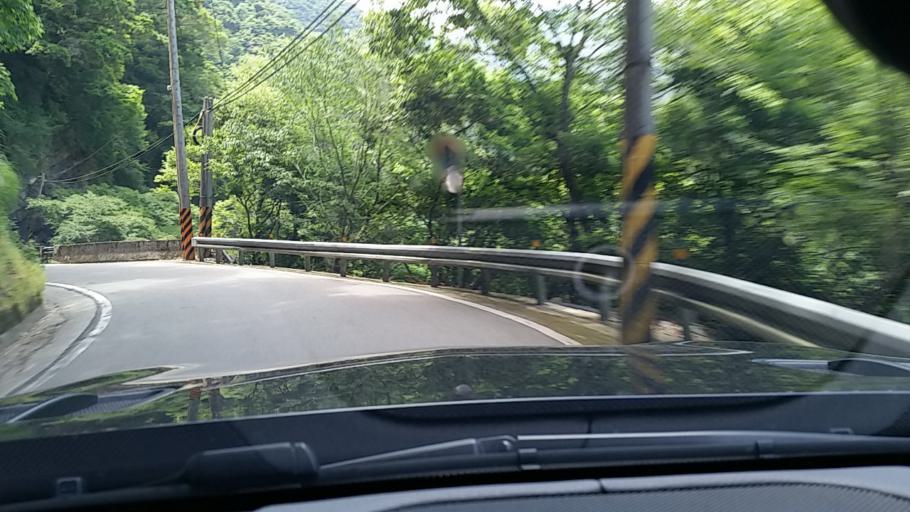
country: TW
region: Taiwan
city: Daxi
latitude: 24.6985
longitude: 121.3696
